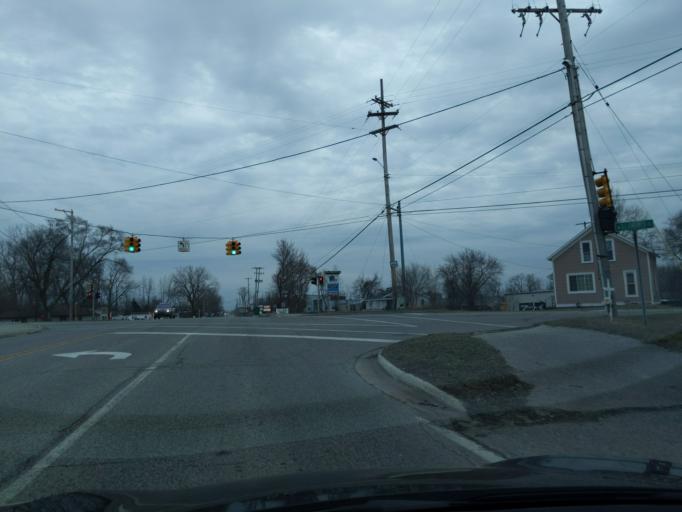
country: US
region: Michigan
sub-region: Bay County
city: Bay City
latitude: 43.6373
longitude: -83.9137
